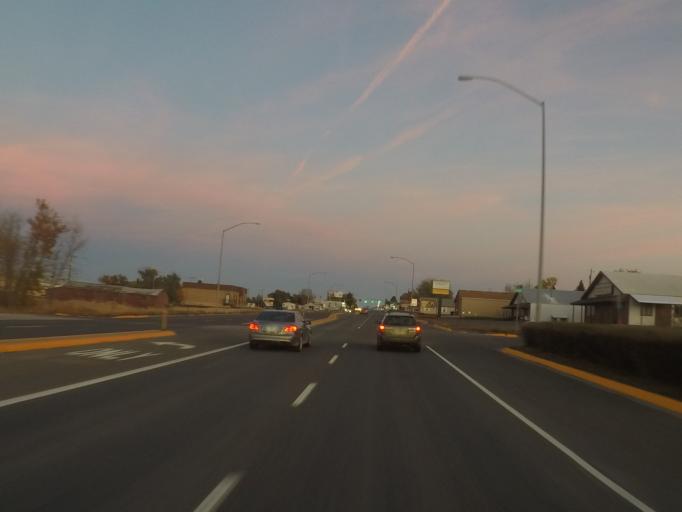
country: US
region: Montana
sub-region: Lewis and Clark County
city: Helena
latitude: 46.6074
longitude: -112.0706
